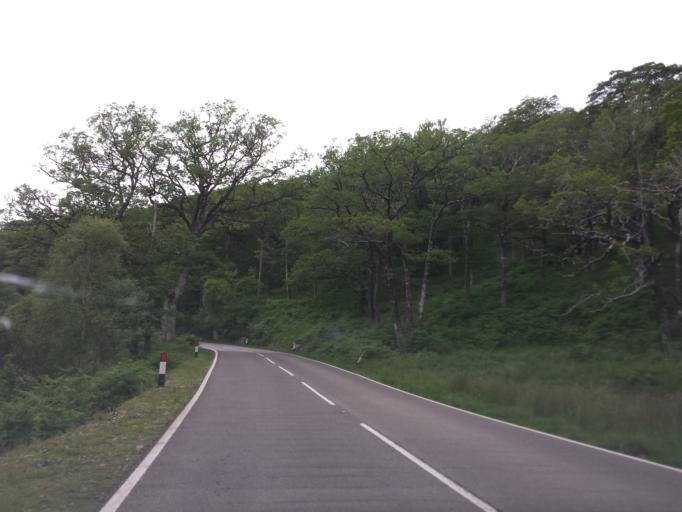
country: GB
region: Scotland
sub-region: Argyll and Bute
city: Isle Of Mull
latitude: 56.9017
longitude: -5.7537
